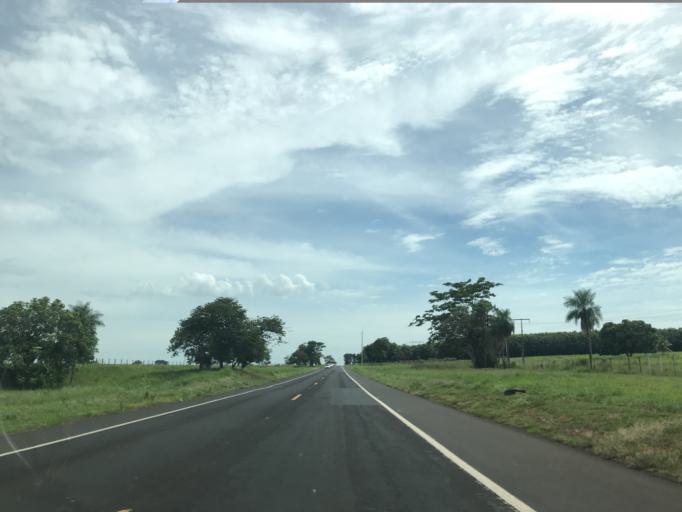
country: BR
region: Sao Paulo
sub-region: Nova Granada
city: Nova Granada
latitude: -20.3995
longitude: -49.2428
